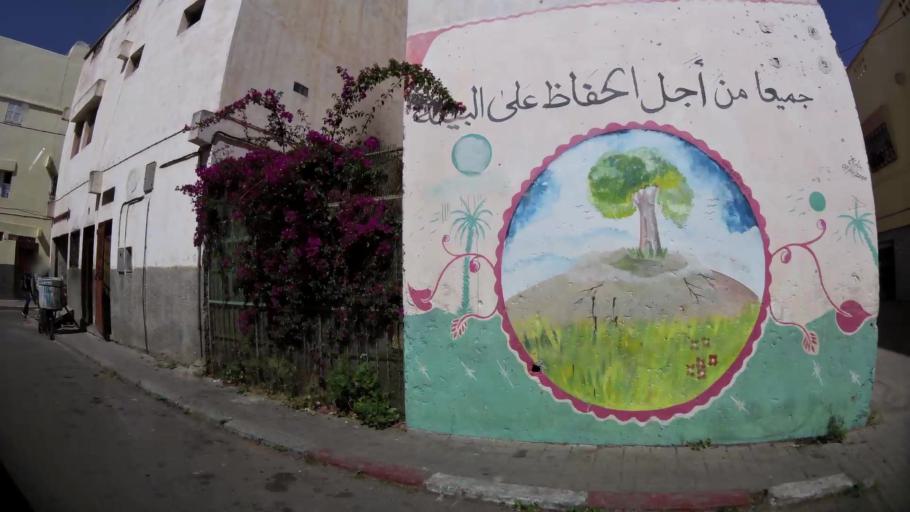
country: MA
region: Souss-Massa-Draa
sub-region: Inezgane-Ait Mellou
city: Inezgane
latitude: 30.3546
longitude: -9.5410
